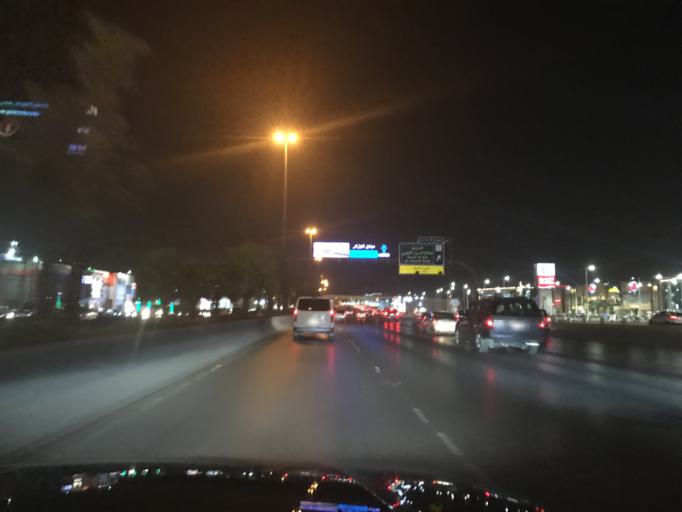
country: SA
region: Ar Riyad
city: Riyadh
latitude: 24.6861
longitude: 46.7764
